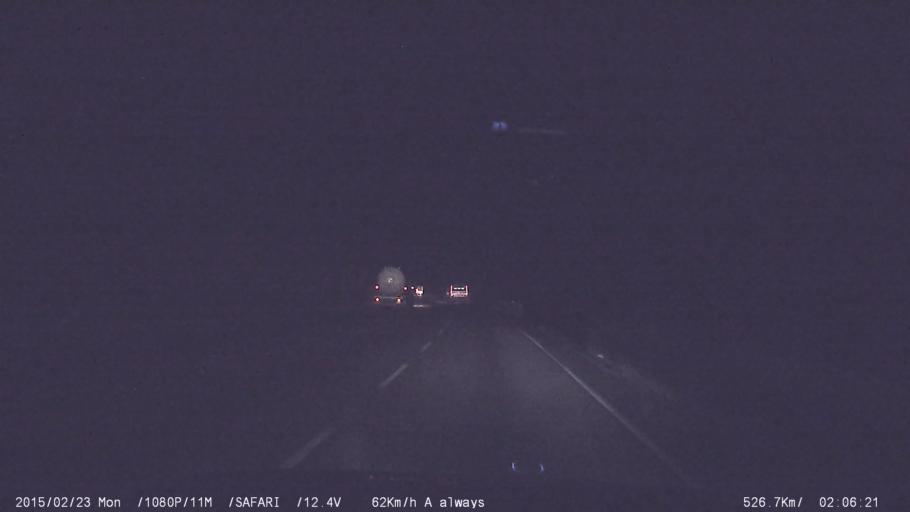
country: IN
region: Tamil Nadu
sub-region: Krishnagiri
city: Kelamangalam
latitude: 12.6571
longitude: 78.0216
